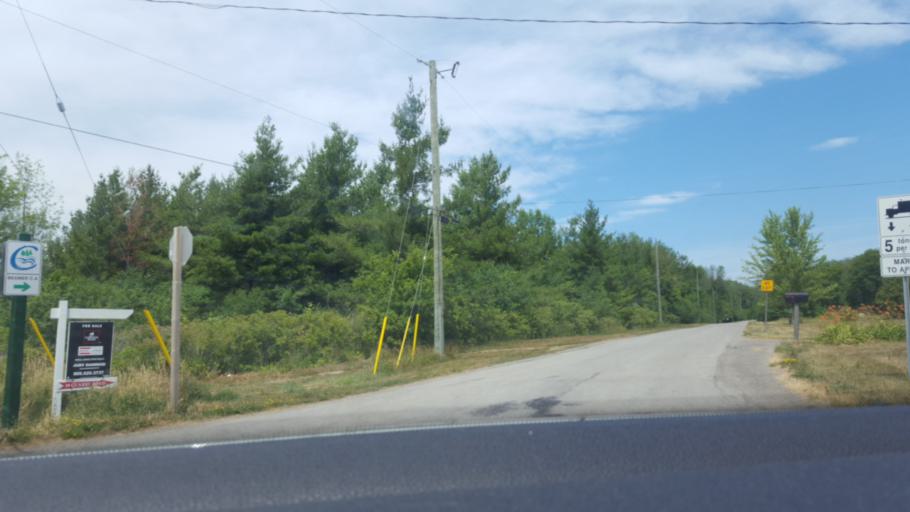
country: CA
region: Ontario
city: Hamilton
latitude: 43.1859
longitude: -79.5769
